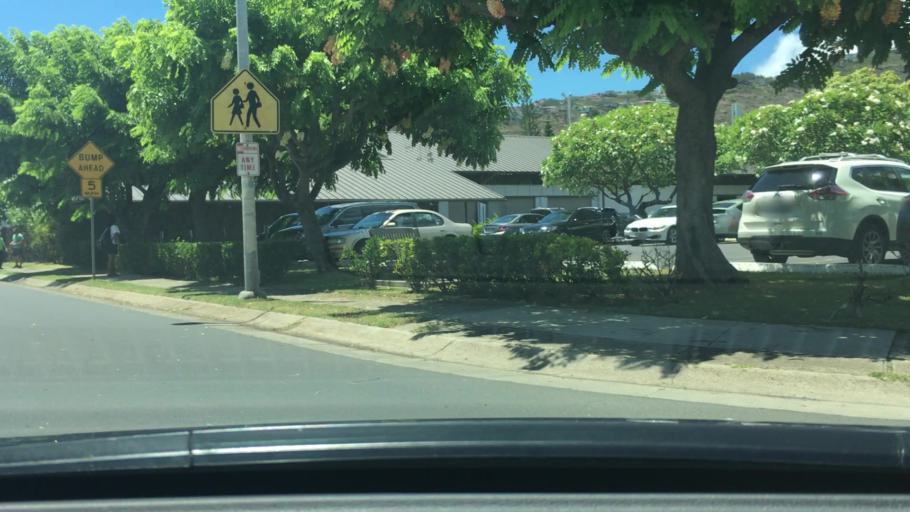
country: US
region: Hawaii
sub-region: Honolulu County
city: Waimanalo
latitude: 21.2790
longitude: -157.7518
